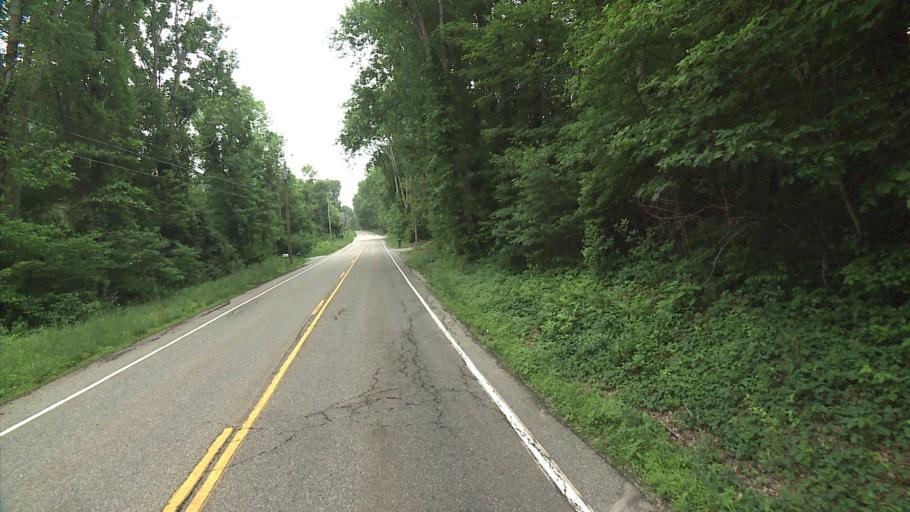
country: US
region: Connecticut
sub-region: Tolland County
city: Hebron
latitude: 41.7105
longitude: -72.3680
